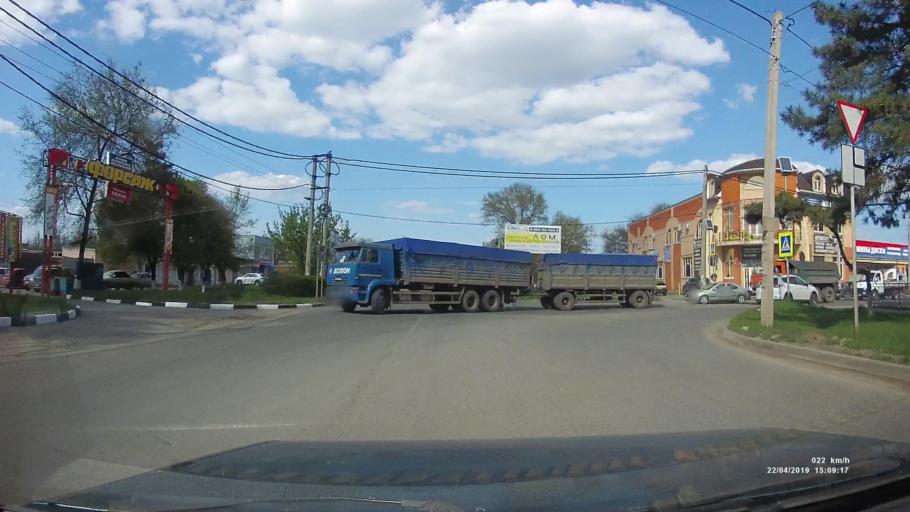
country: RU
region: Rostov
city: Azov
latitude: 47.0997
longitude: 39.4112
